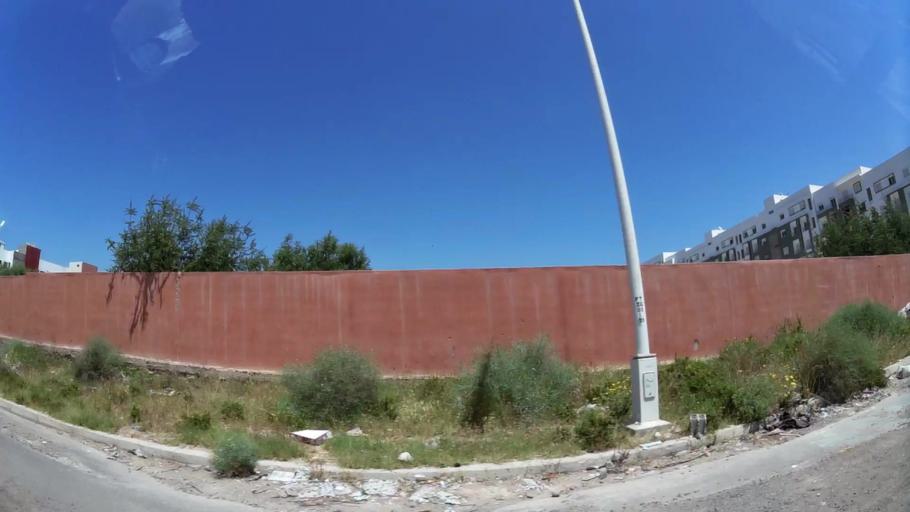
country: MA
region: Oued ed Dahab-Lagouira
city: Dakhla
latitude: 30.4394
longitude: -9.5615
